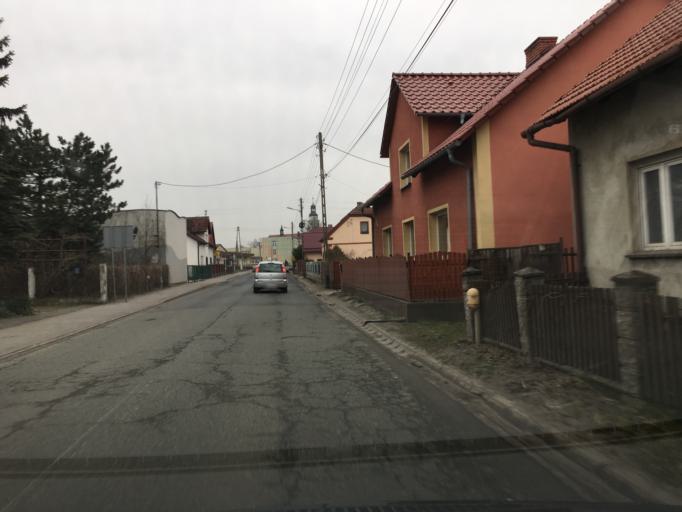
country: PL
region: Opole Voivodeship
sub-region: Powiat kedzierzynsko-kozielski
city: Bierawa
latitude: 50.2821
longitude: 18.2416
